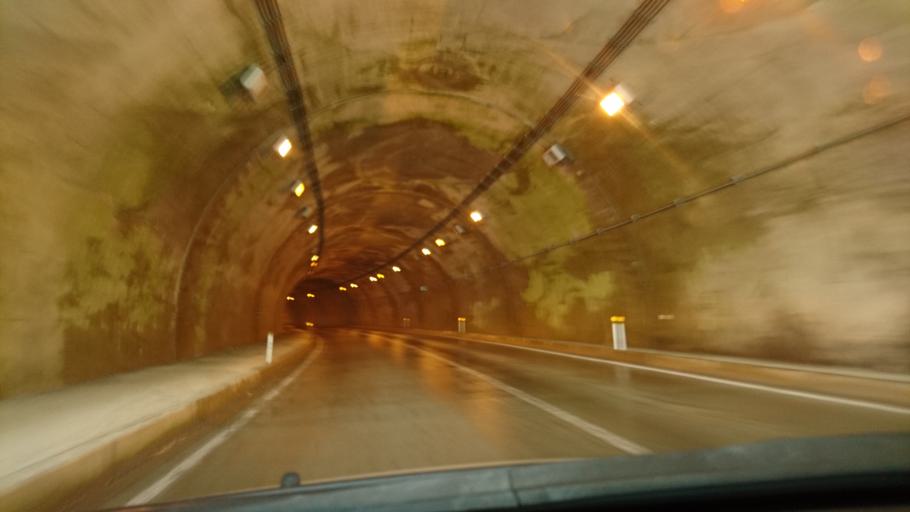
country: JP
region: Iwate
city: Mizusawa
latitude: 39.1257
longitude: 140.9195
